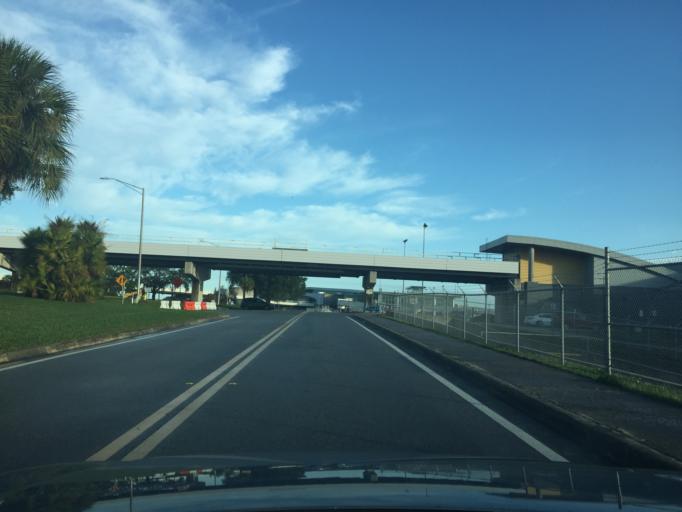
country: US
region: Florida
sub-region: Hillsborough County
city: Egypt Lake-Leto
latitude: 27.9793
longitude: -82.5324
